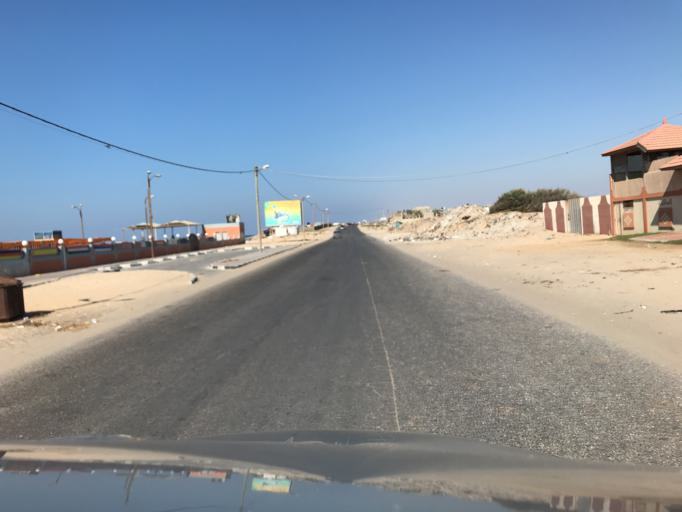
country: PS
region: Gaza Strip
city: Dayr al Balah
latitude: 31.4300
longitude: 34.3435
